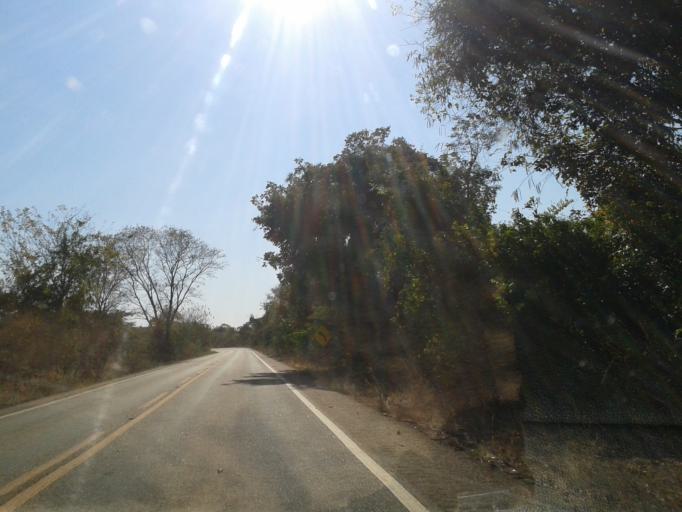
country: BR
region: Goias
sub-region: Mozarlandia
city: Mozarlandia
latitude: -14.6531
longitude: -50.5231
